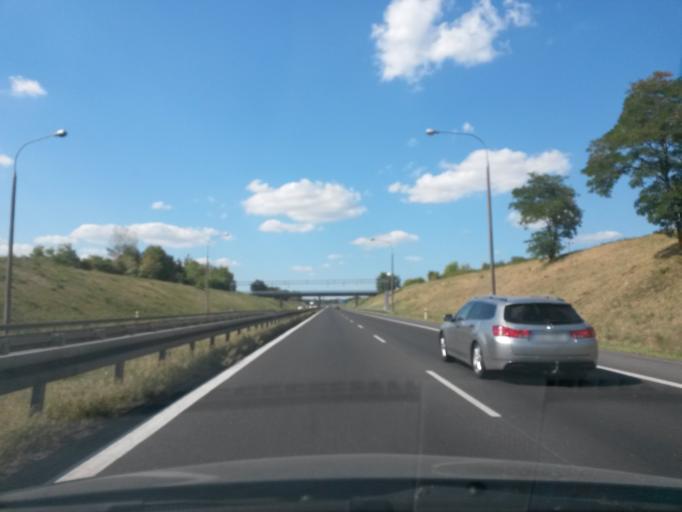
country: PL
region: Masovian Voivodeship
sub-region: Powiat nowodworski
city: Zakroczym
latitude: 52.4323
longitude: 20.6516
